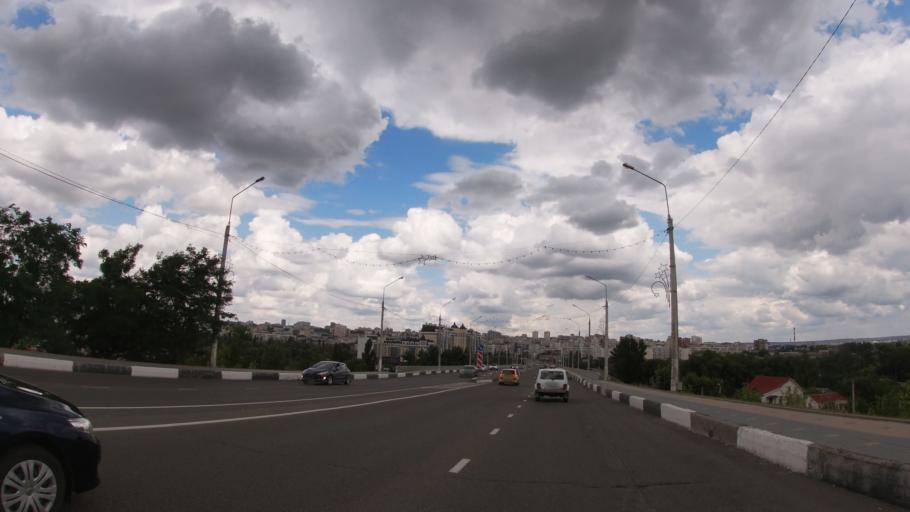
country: RU
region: Belgorod
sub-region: Belgorodskiy Rayon
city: Belgorod
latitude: 50.5848
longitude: 36.5861
